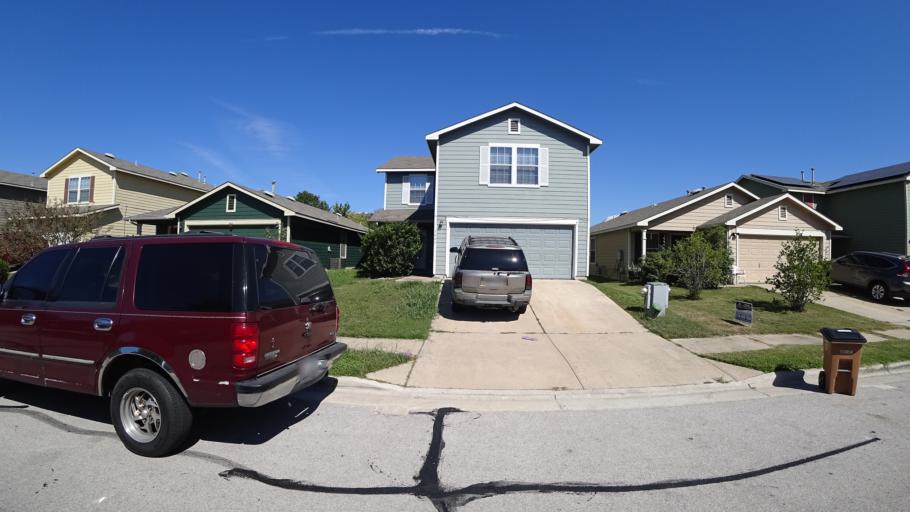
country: US
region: Texas
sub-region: Travis County
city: Austin
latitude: 30.1991
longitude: -97.6942
